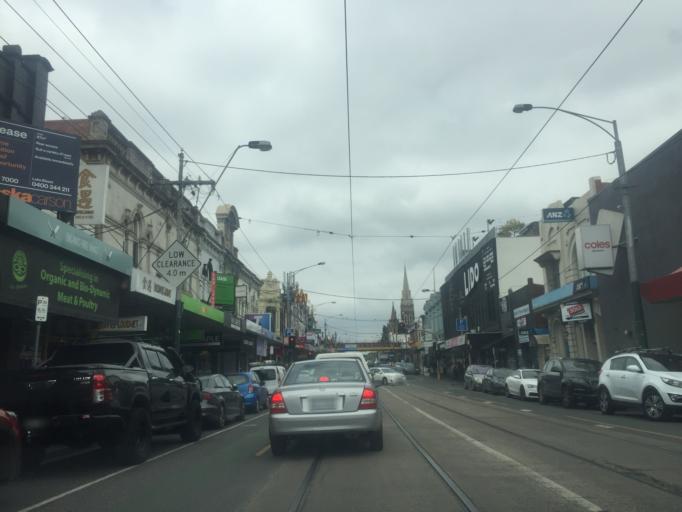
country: AU
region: Victoria
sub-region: Boroondara
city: Hawthorn East
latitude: -37.8199
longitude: 145.0359
